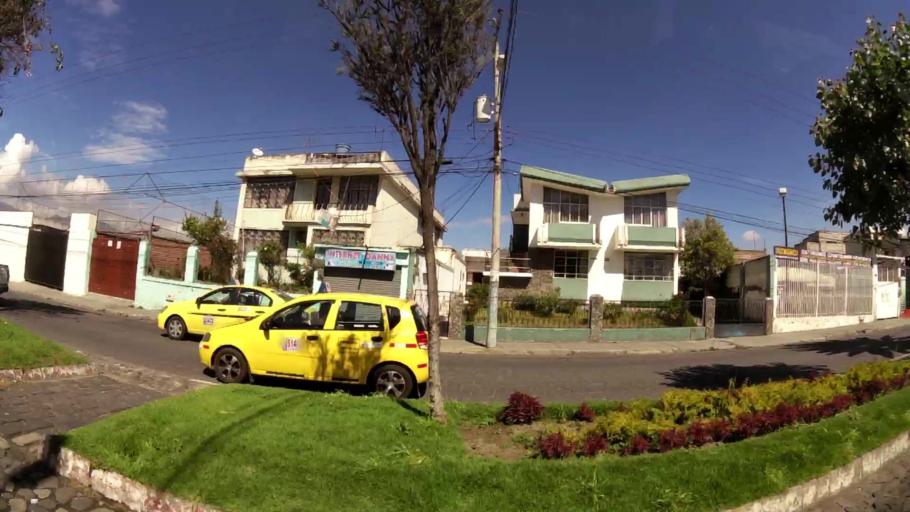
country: EC
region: Chimborazo
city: Riobamba
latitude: -1.6606
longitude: -78.6622
